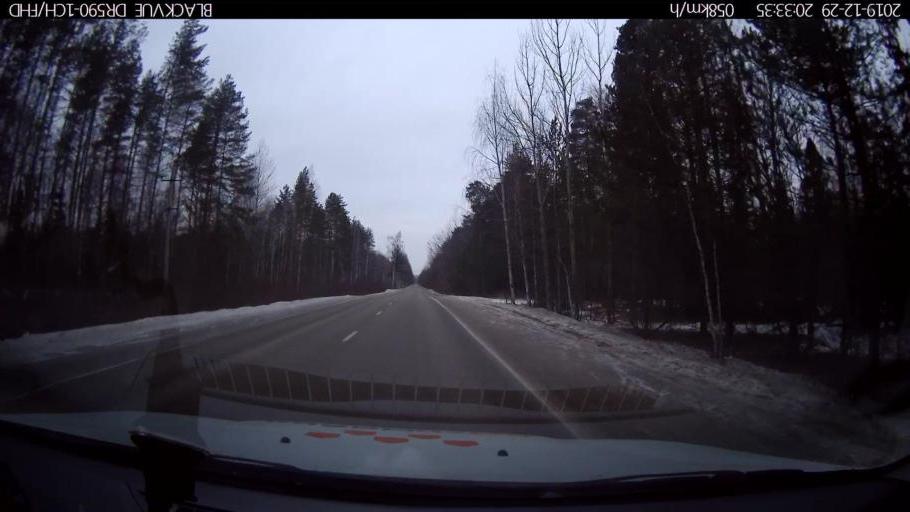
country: RU
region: Nizjnij Novgorod
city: Afonino
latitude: 56.1812
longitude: 44.0503
